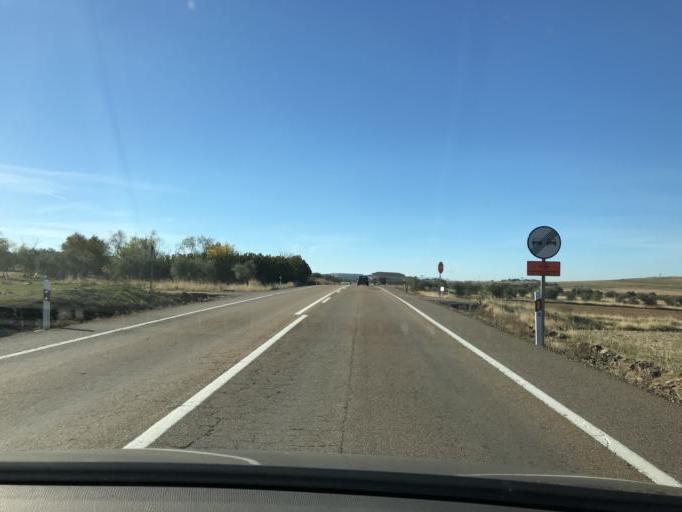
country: ES
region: Extremadura
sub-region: Provincia de Badajoz
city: Azuaga
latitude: 38.2671
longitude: -5.6906
